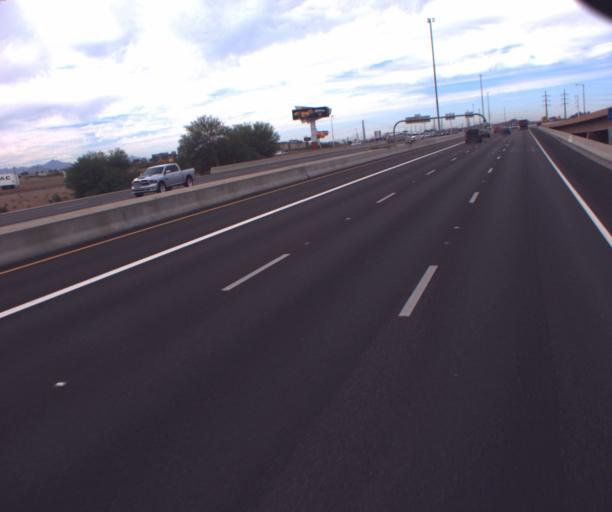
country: US
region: Arizona
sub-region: Maricopa County
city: Tempe
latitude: 33.4350
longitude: -111.8945
